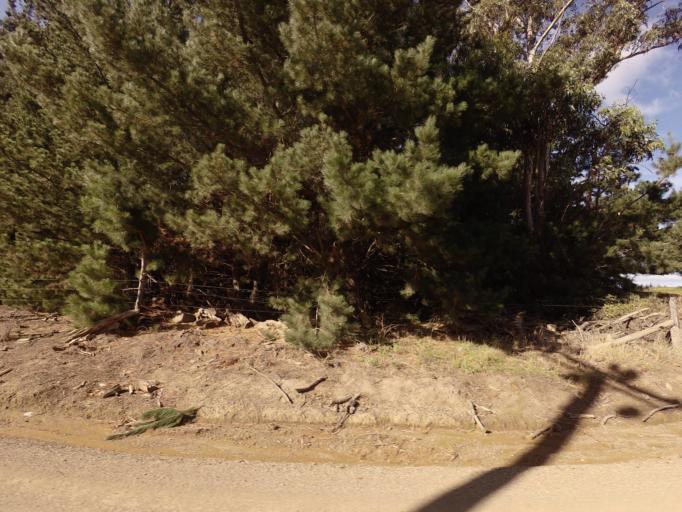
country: AU
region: Tasmania
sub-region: Clarence
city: Sandford
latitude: -43.1484
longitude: 147.7641
